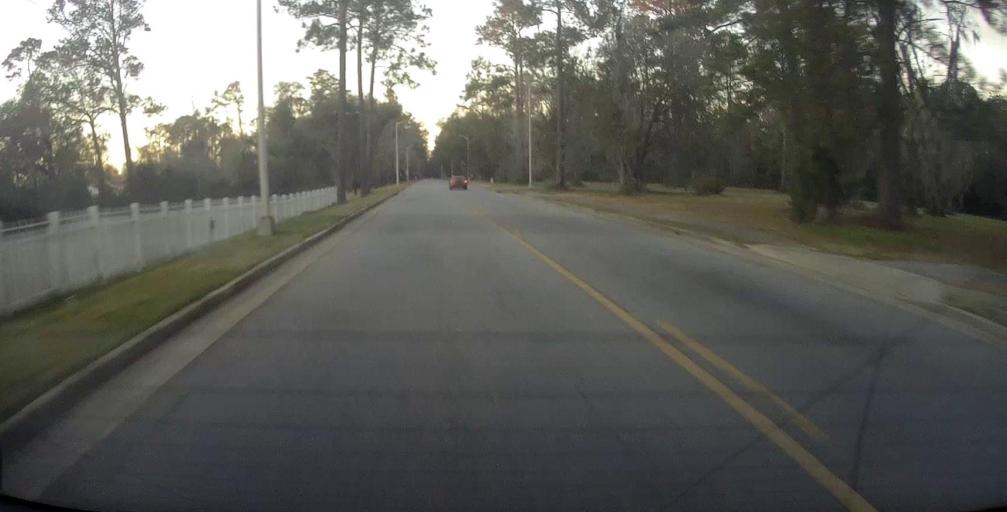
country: US
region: Georgia
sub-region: Dougherty County
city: Albany
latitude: 31.5287
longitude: -84.1367
